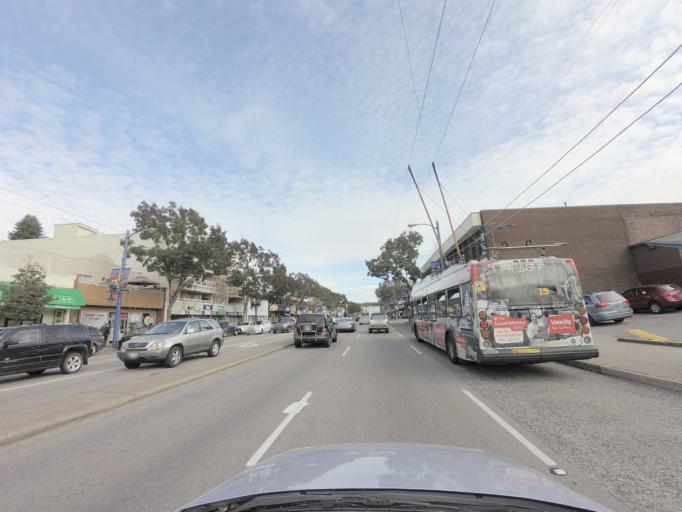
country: CA
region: British Columbia
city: Vancouver
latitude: 49.2339
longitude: -123.0355
